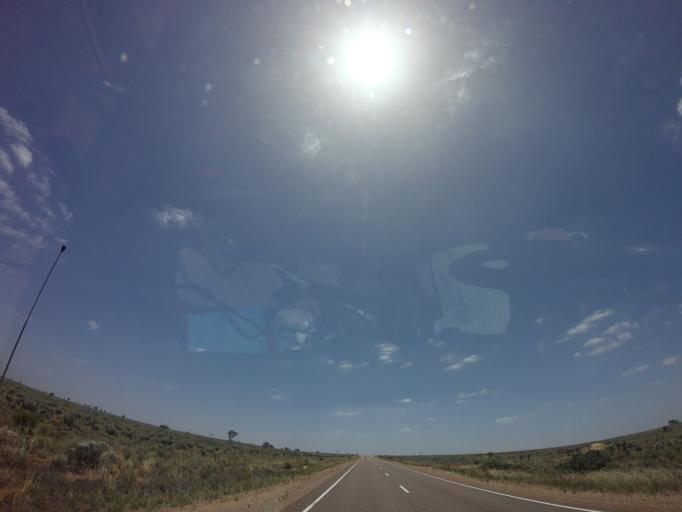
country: AU
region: South Australia
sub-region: Whyalla
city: Whyalla
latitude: -32.8410
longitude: 137.0255
